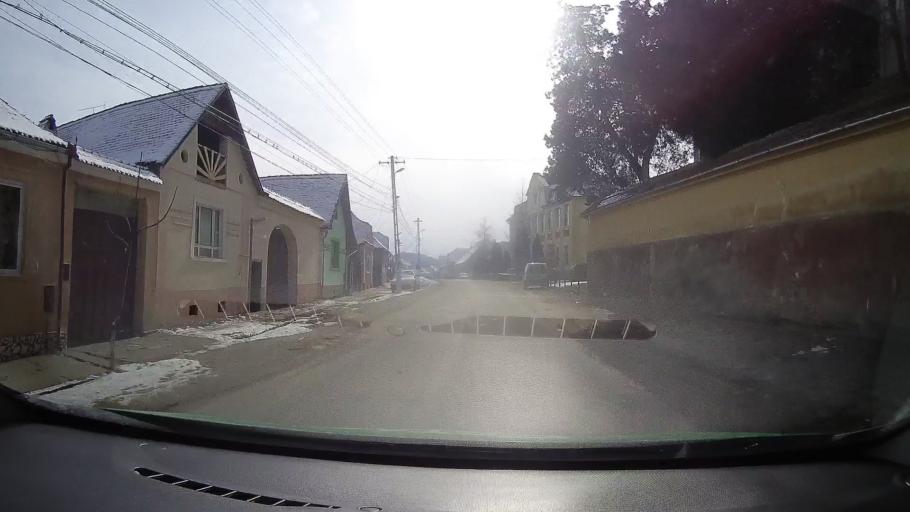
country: RO
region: Sibiu
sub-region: Comuna Laslea
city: Laslea
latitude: 46.2103
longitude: 24.6571
